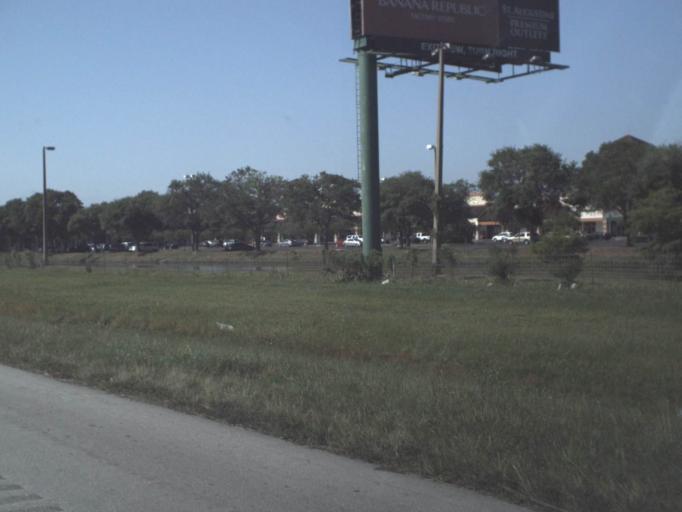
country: US
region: Florida
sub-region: Saint Johns County
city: Saint Augustine
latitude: 29.9241
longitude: -81.4152
